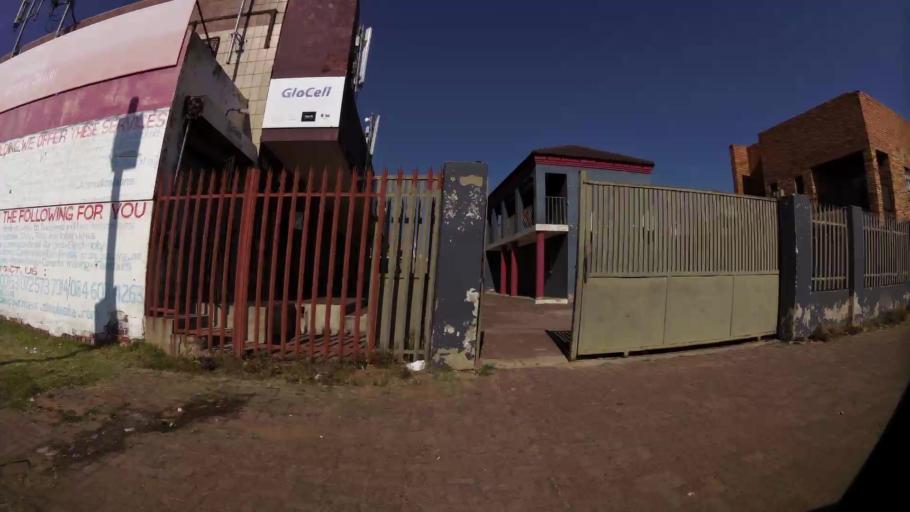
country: ZA
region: Gauteng
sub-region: City of Johannesburg Metropolitan Municipality
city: Johannesburg
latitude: -26.2470
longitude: 27.9569
